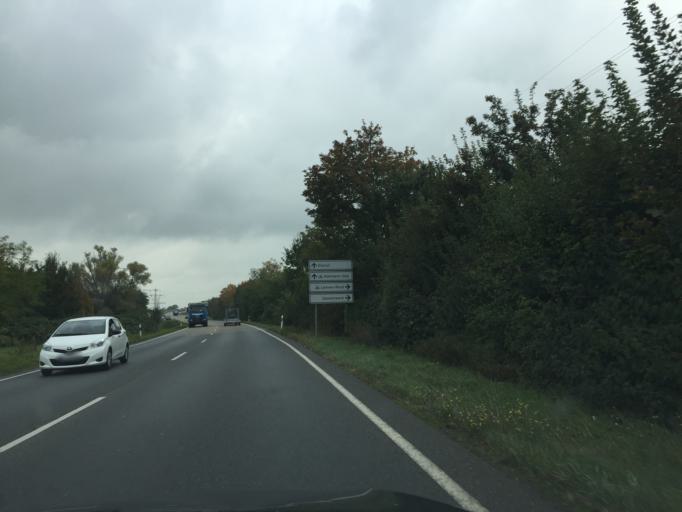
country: DE
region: Baden-Wuerttemberg
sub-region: Karlsruhe Region
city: Leimen
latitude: 49.3500
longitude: 8.6759
